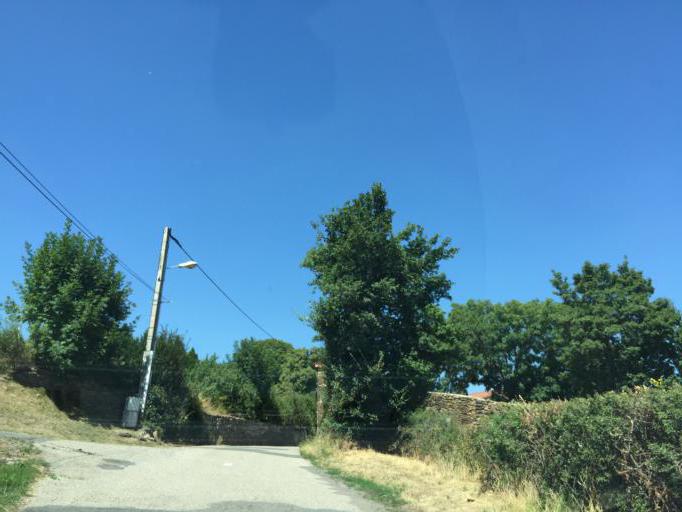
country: FR
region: Rhone-Alpes
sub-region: Departement de la Loire
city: Saint-Jean-Bonnefonds
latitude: 45.4617
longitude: 4.4580
